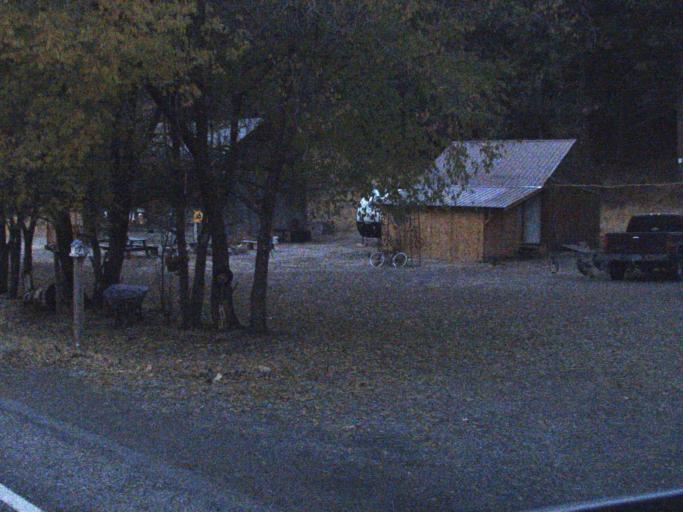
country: US
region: Washington
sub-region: Ferry County
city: Republic
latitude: 48.5703
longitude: -118.7475
